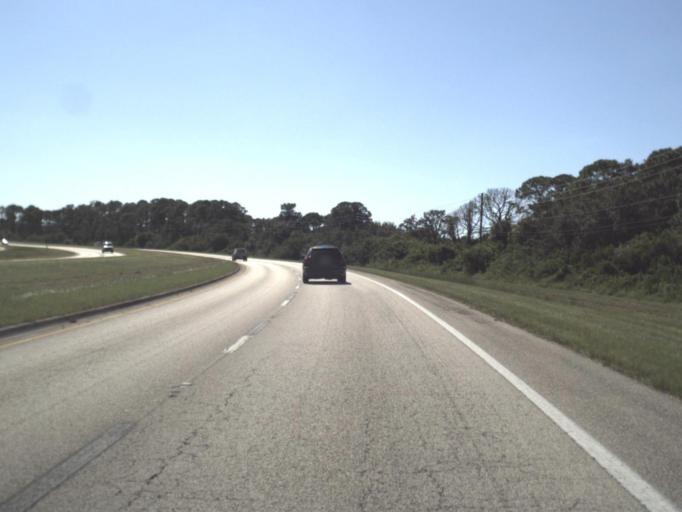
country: US
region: Florida
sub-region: Sarasota County
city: North Port
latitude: 26.9939
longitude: -82.2020
